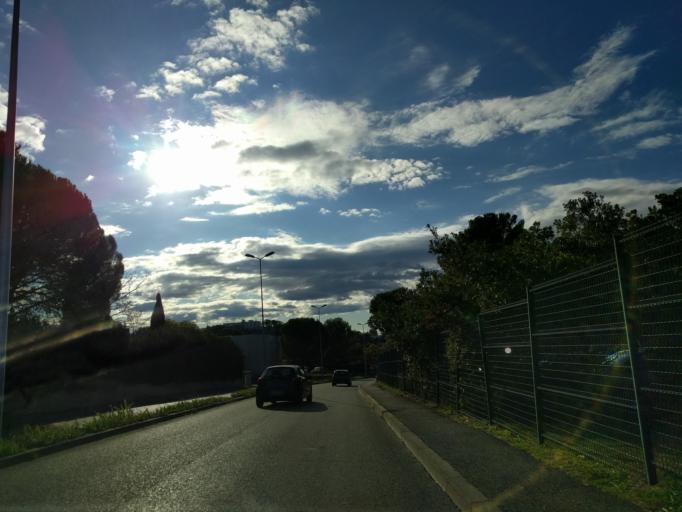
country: FR
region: Languedoc-Roussillon
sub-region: Departement de l'Herault
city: Montferrier-sur-Lez
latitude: 43.6434
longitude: 3.8390
